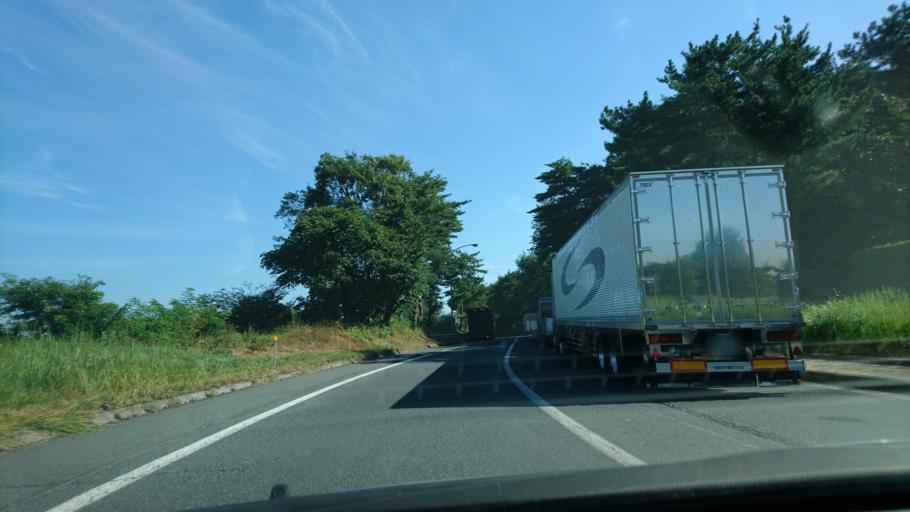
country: JP
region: Iwate
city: Mizusawa
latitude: 39.0679
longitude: 141.0990
